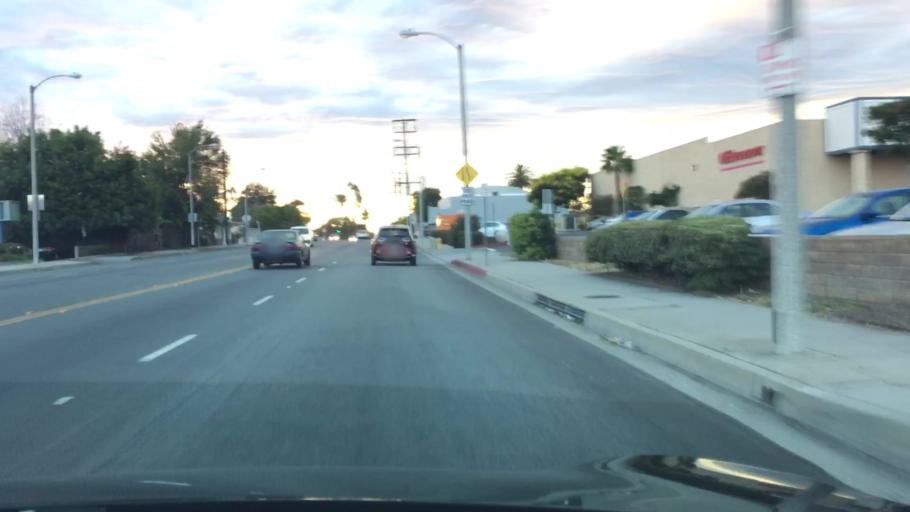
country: US
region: California
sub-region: Los Angeles County
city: Temple City
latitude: 34.0991
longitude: -118.0741
